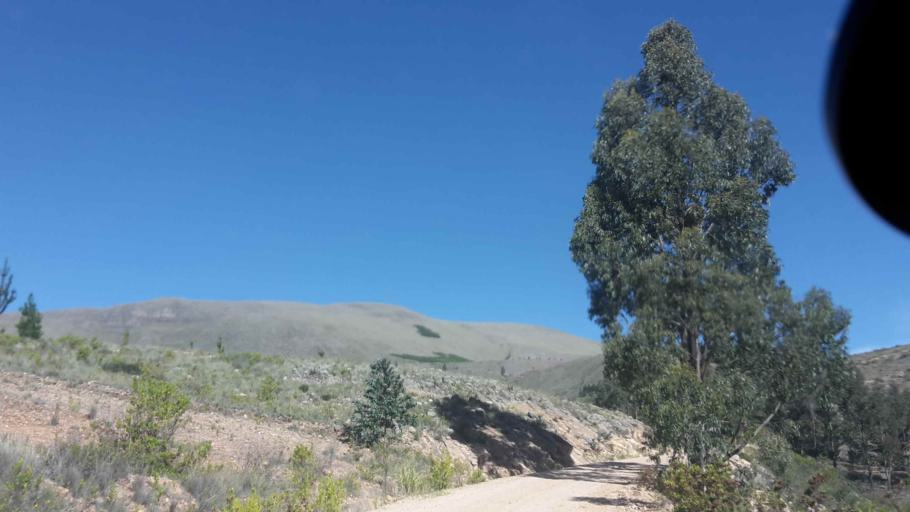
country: BO
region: Cochabamba
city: Arani
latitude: -17.6605
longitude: -65.7359
